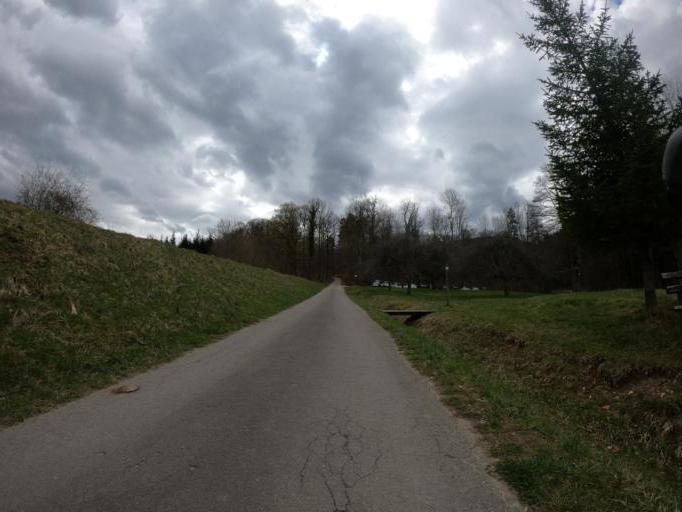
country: DE
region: Baden-Wuerttemberg
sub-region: Tuebingen Region
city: Mossingen
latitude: 48.3853
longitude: 9.0534
